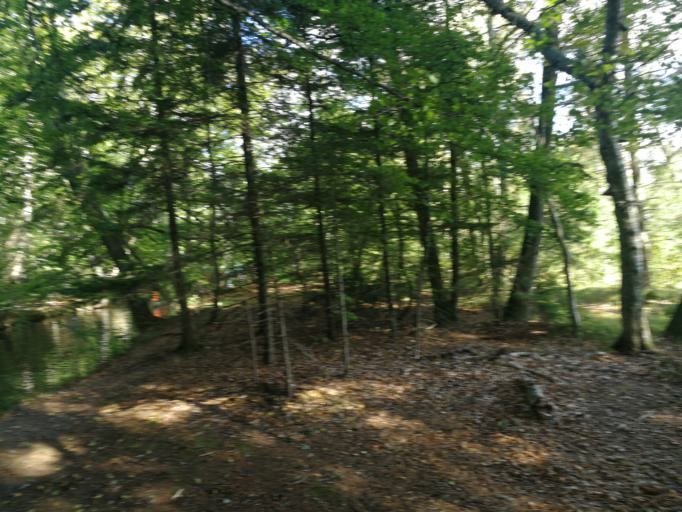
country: DK
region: Central Jutland
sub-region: Silkeborg Kommune
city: Virklund
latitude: 56.1450
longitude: 9.5759
